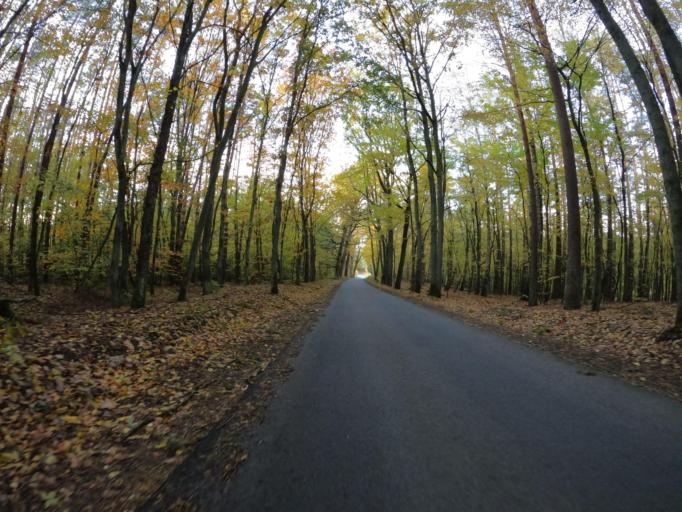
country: PL
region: West Pomeranian Voivodeship
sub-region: Powiat mysliborski
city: Barlinek
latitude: 52.9310
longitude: 15.2866
